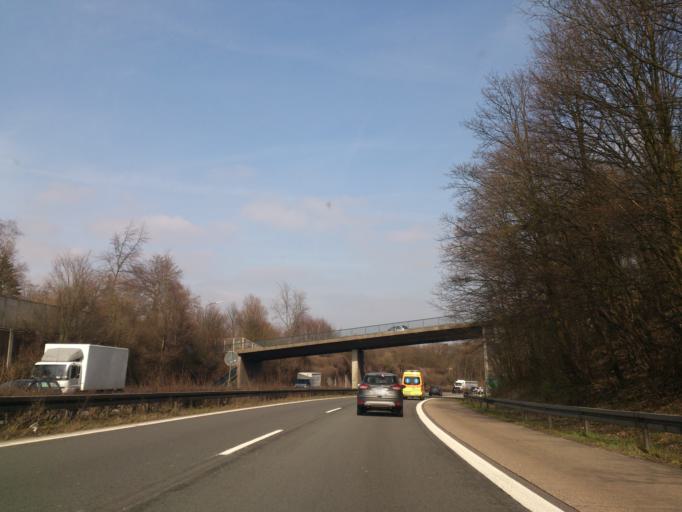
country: DE
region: North Rhine-Westphalia
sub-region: Regierungsbezirk Dusseldorf
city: Solingen
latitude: 51.2240
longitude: 7.0743
